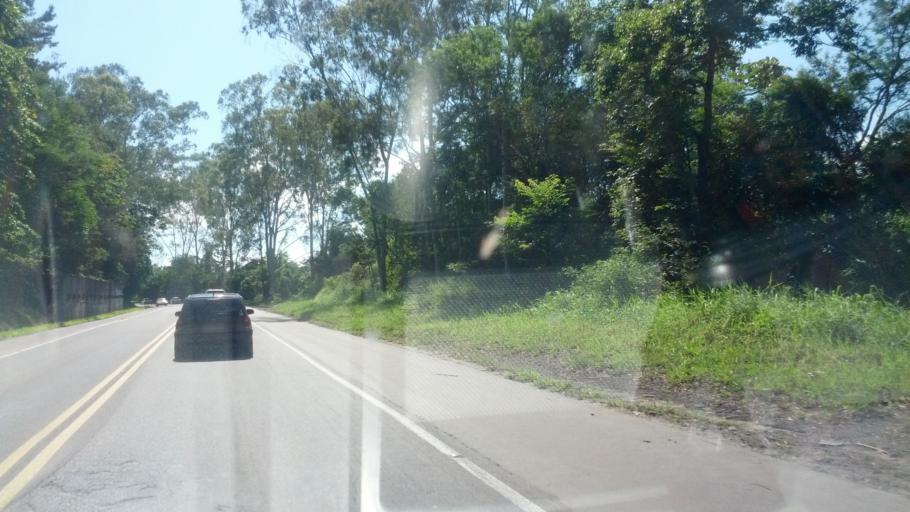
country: BR
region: Santa Catarina
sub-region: Ibirama
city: Ibirama
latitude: -27.1471
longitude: -49.5534
